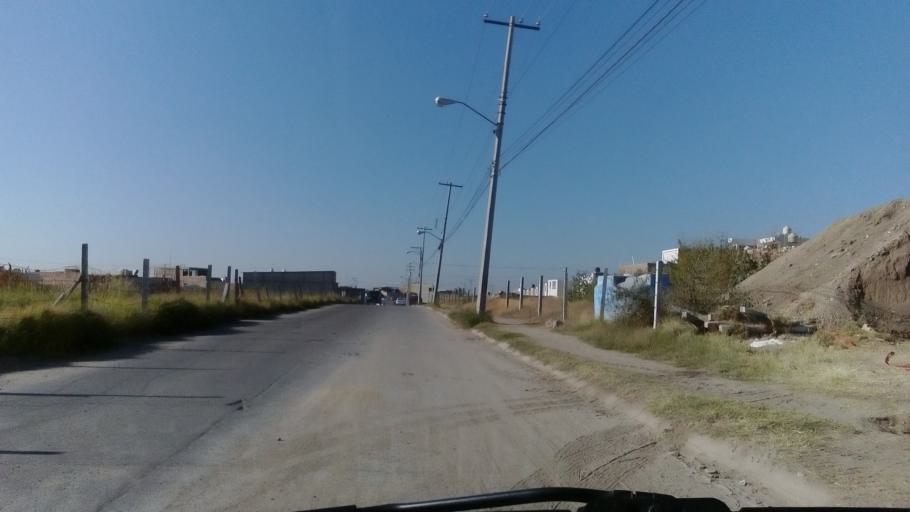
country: MX
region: Guanajuato
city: Leon
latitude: 21.1114
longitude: -101.7083
